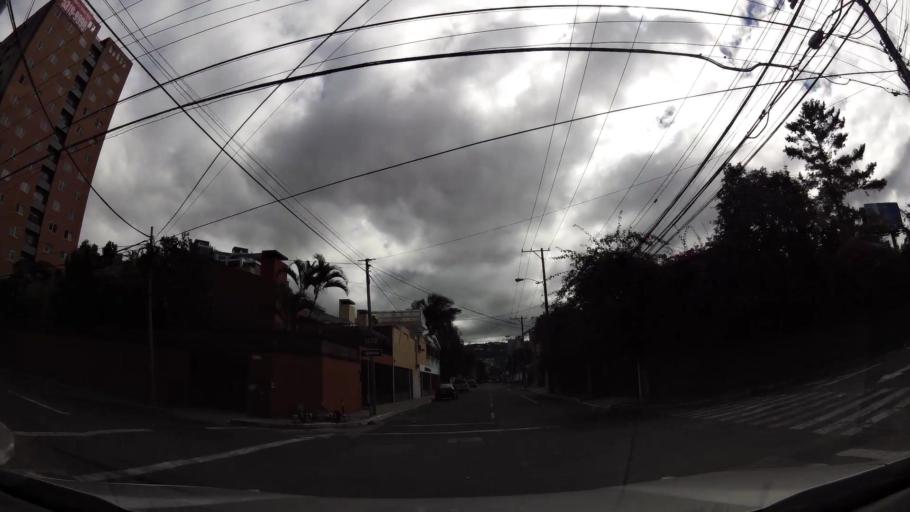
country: GT
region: Guatemala
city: Santa Catarina Pinula
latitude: 14.5911
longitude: -90.5057
